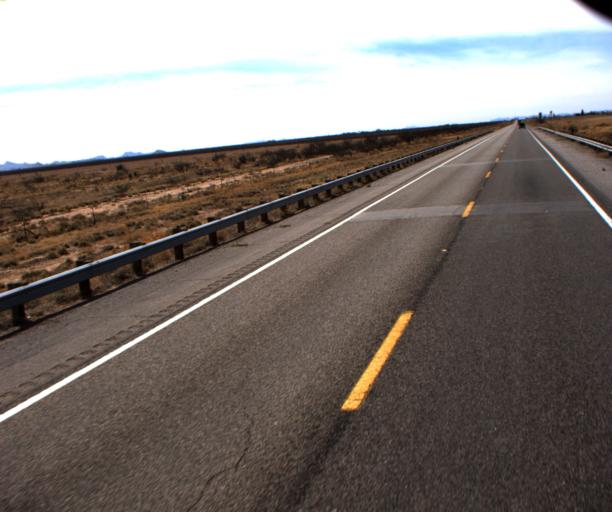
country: US
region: Arizona
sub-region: Cochise County
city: Pirtleville
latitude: 31.6438
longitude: -109.6727
